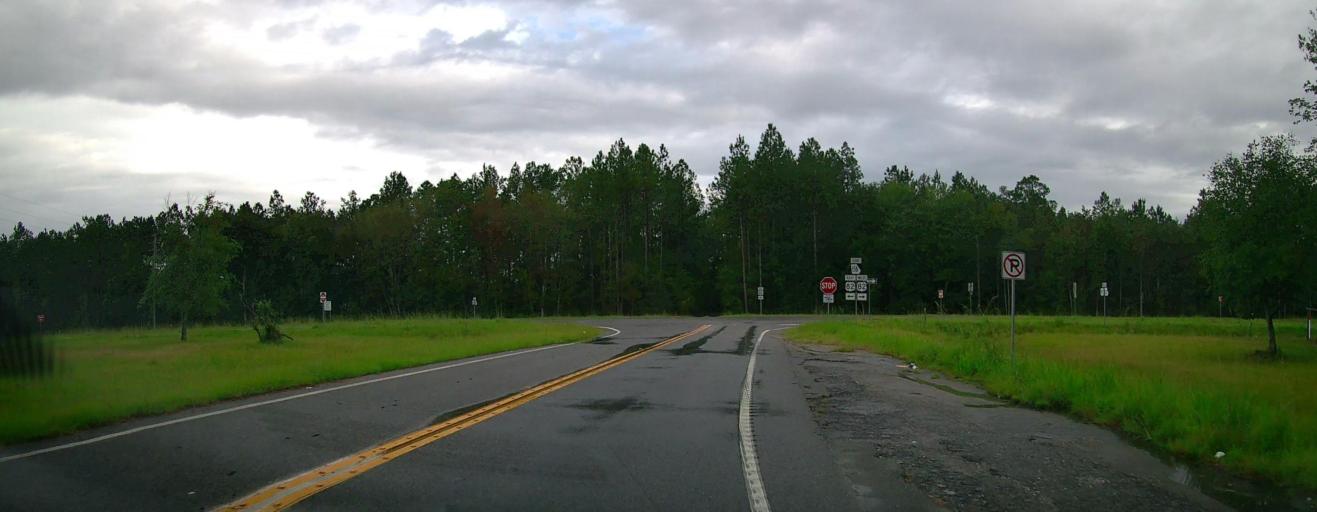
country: US
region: Georgia
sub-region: Ware County
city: Deenwood
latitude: 31.2628
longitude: -82.5180
